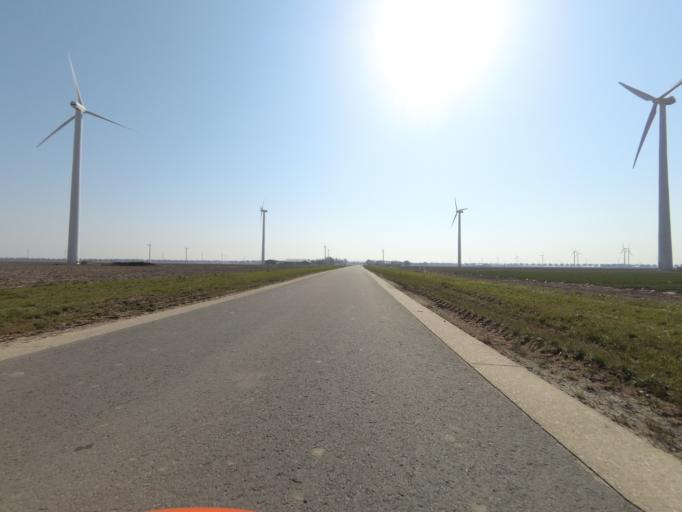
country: NL
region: Utrecht
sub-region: Gemeente Bunschoten
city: Spakenburg
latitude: 52.3351
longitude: 5.3858
